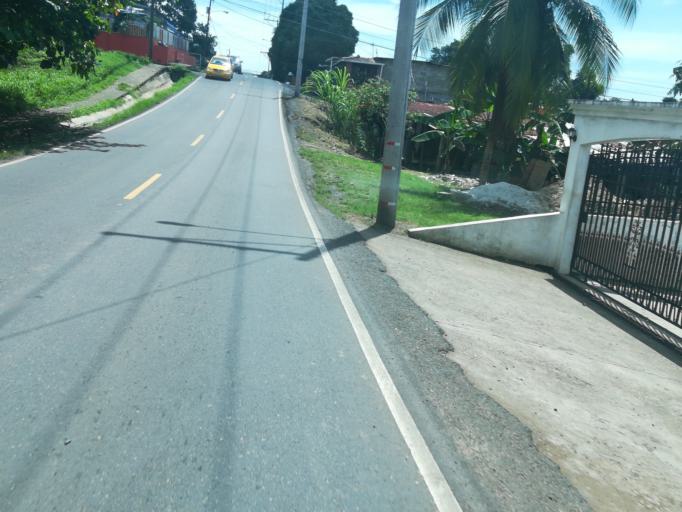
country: PA
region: Panama
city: Tocumen
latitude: 9.0926
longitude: -79.4025
